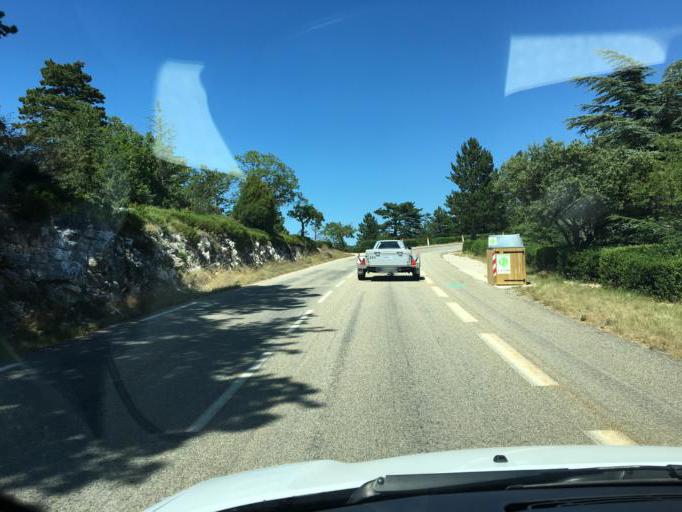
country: FR
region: Provence-Alpes-Cote d'Azur
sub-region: Departement du Vaucluse
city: Bedoin
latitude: 44.1691
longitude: 5.1957
